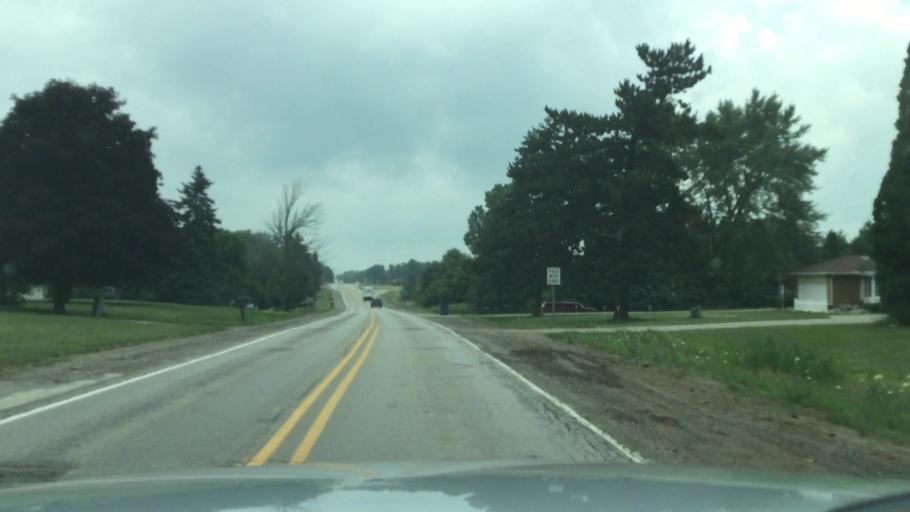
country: US
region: Michigan
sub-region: Shiawassee County
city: Durand
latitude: 42.9589
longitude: -83.9290
